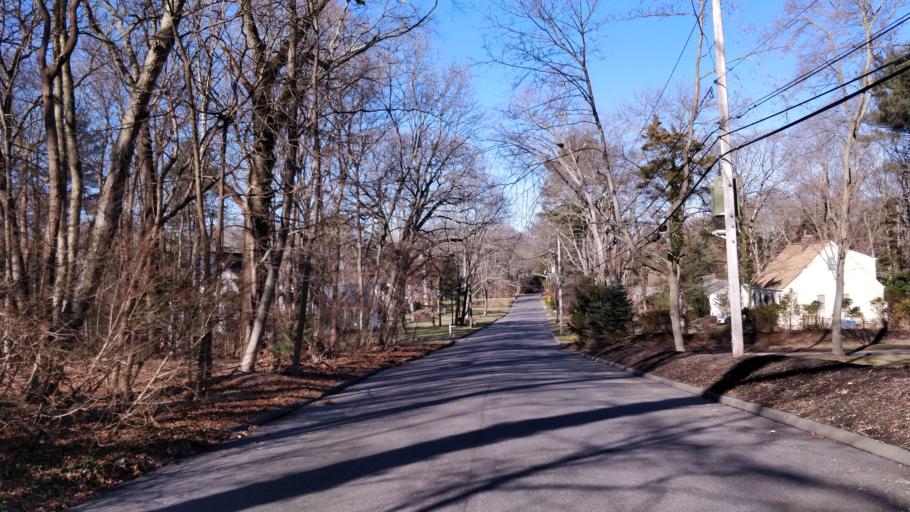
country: US
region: New York
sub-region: Suffolk County
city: Smithtown
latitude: 40.8587
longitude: -73.2031
